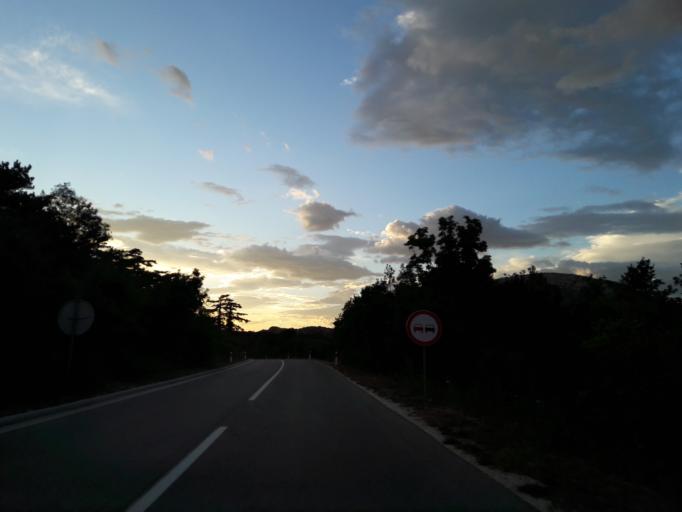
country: HR
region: Dubrovacko-Neretvanska
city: Orebic
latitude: 42.9660
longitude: 17.3070
